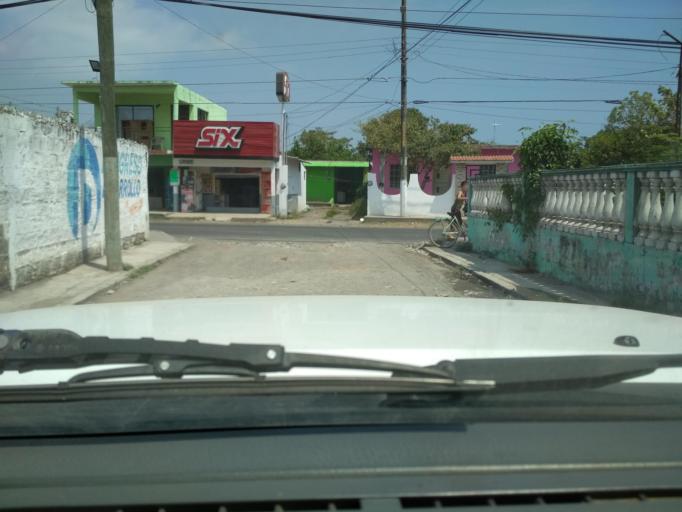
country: MX
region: Veracruz
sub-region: Medellin
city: Fraccionamiento Arboledas San Ramon
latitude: 19.0943
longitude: -96.1442
